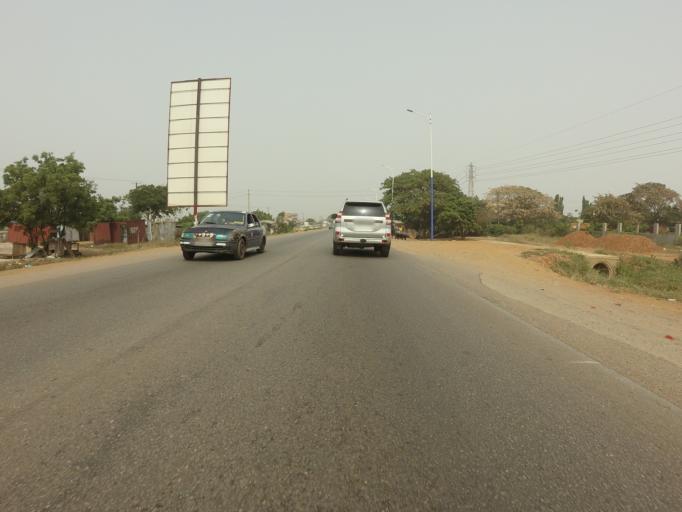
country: GH
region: Greater Accra
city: Tema
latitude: 5.7511
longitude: 0.0437
